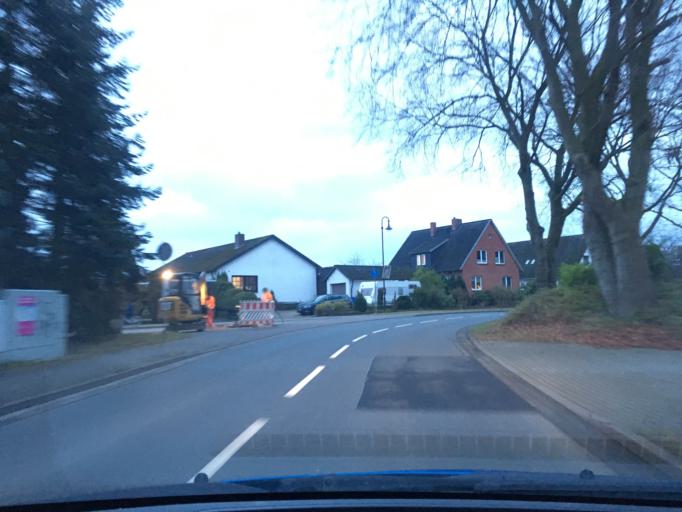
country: DE
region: Lower Saxony
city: Vogelsen
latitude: 53.2915
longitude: 10.3616
